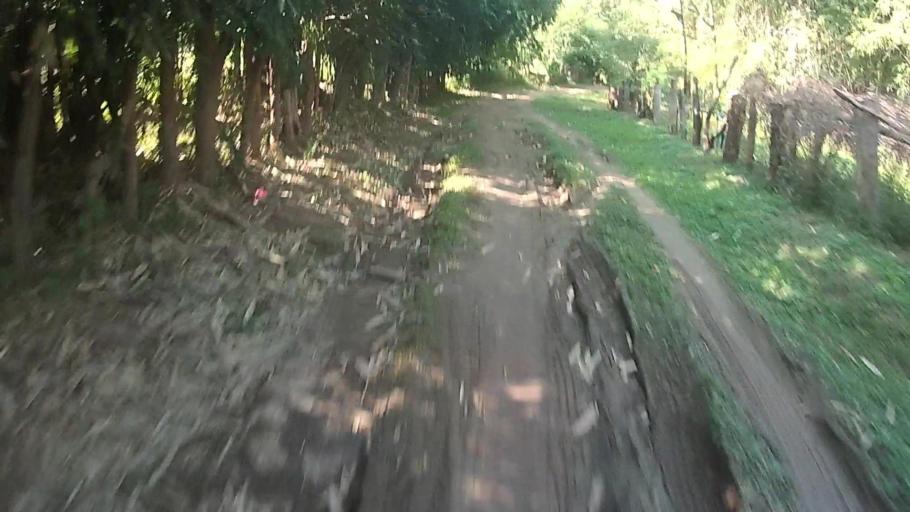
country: TH
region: Chiang Mai
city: Mae On
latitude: 18.9329
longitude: 99.2001
